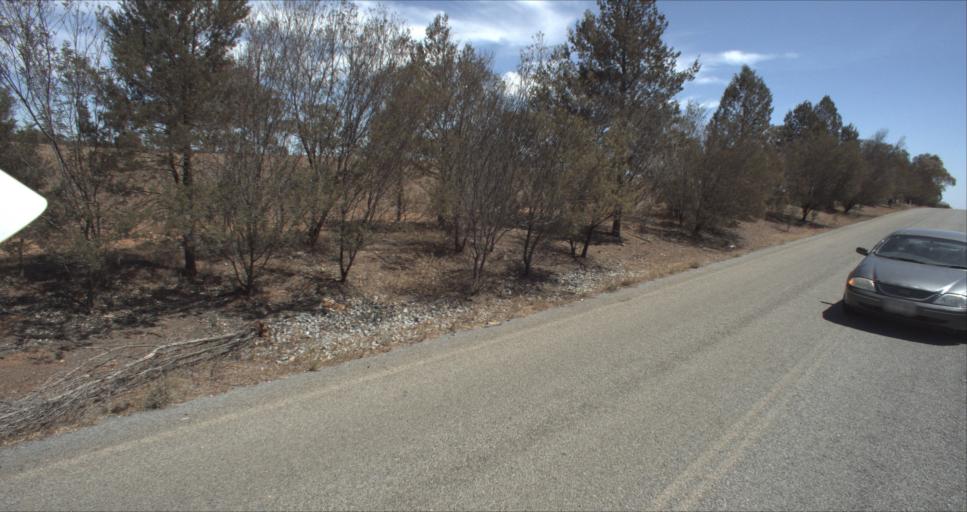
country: AU
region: New South Wales
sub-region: Leeton
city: Leeton
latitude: -34.5898
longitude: 146.4515
